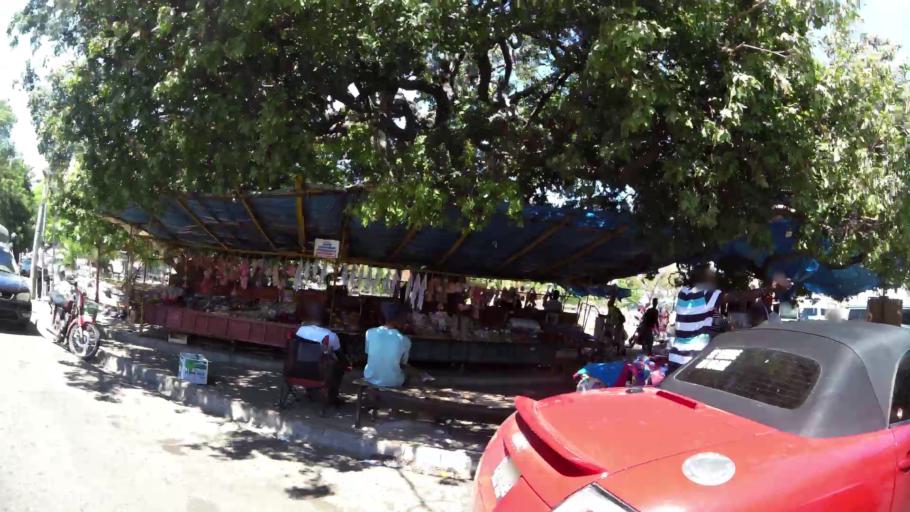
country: DO
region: Santiago
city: Santiago de los Caballeros
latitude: 19.4548
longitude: -70.7054
